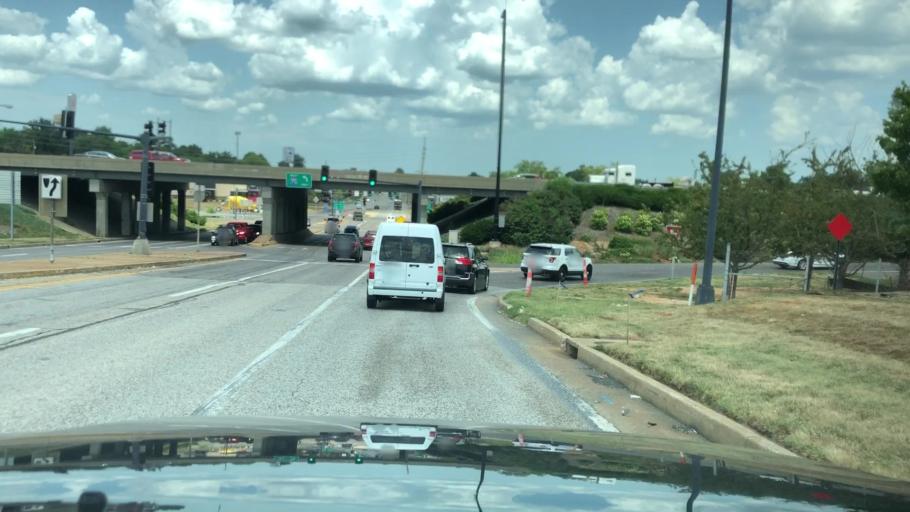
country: US
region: Missouri
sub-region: Saint Charles County
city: O'Fallon
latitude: 38.8016
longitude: -90.7001
